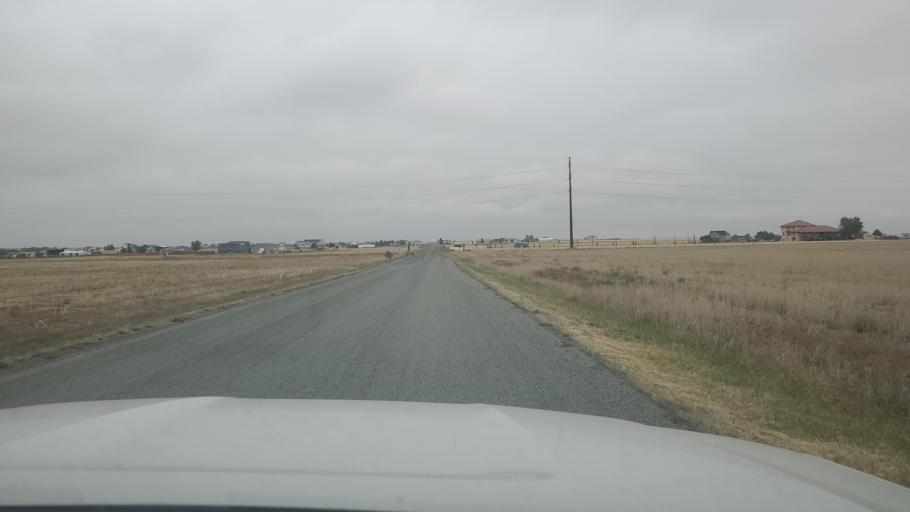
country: US
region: Colorado
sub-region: Weld County
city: Lochbuie
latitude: 39.9404
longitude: -104.6028
